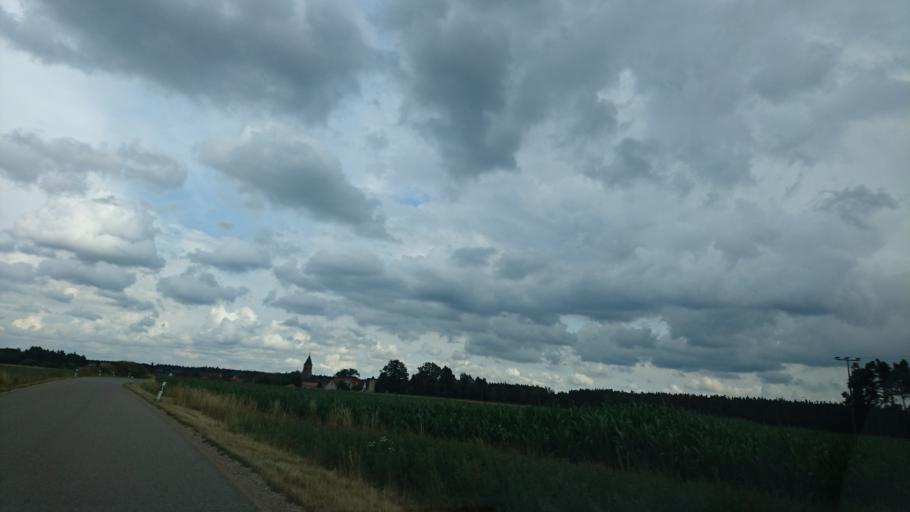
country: DE
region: Bavaria
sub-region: Regierungsbezirk Mittelfranken
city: Roth
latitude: 49.1943
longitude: 11.1032
